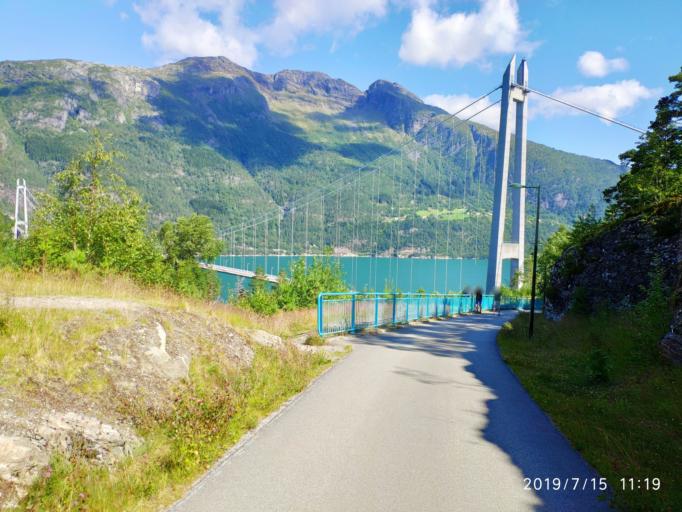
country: NO
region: Hordaland
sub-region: Ulvik
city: Ulvik
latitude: 60.4713
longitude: 6.8346
